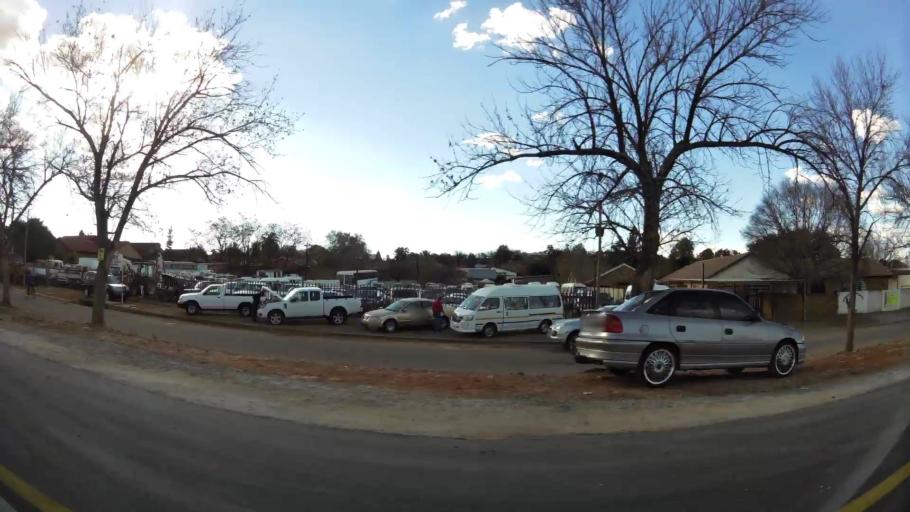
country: ZA
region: North-West
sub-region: Dr Kenneth Kaunda District Municipality
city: Klerksdorp
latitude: -26.8644
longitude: 26.6492
